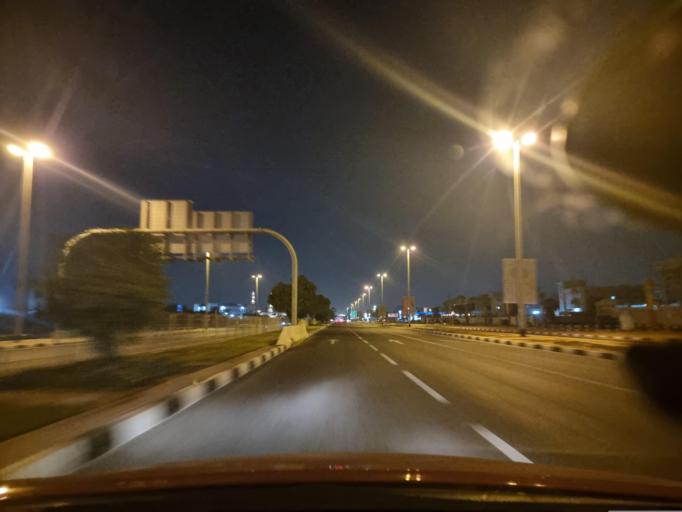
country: AE
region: Ash Shariqah
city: Sharjah
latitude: 25.3549
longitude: 55.4489
